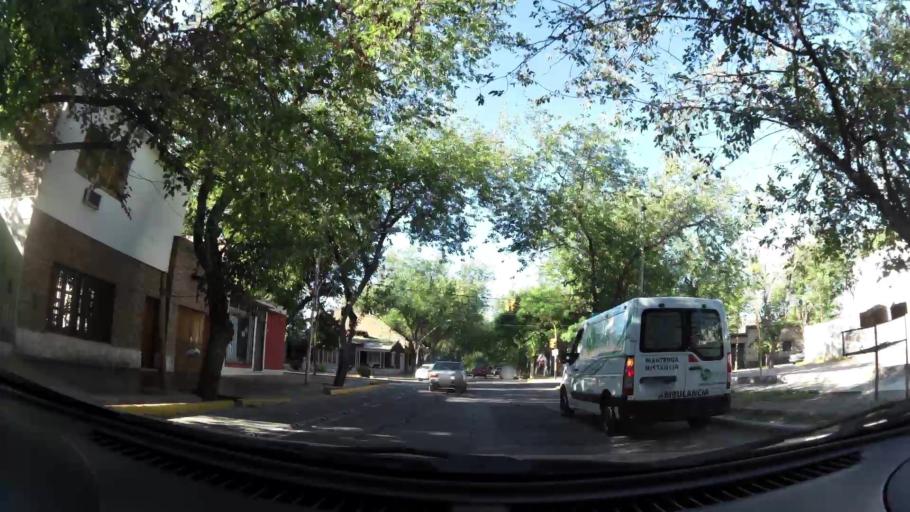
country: AR
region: Mendoza
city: Mendoza
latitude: -32.8741
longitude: -68.8262
